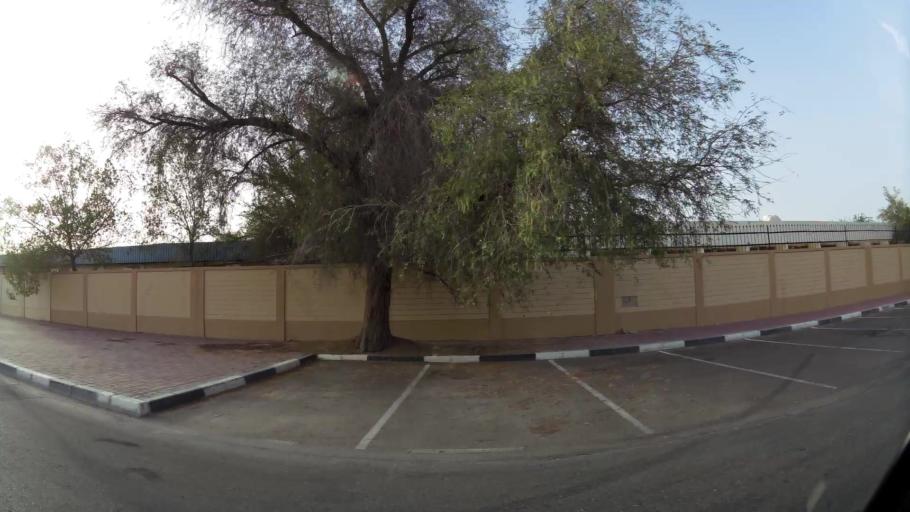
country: OM
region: Al Buraimi
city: Al Buraymi
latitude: 24.2438
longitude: 55.7459
